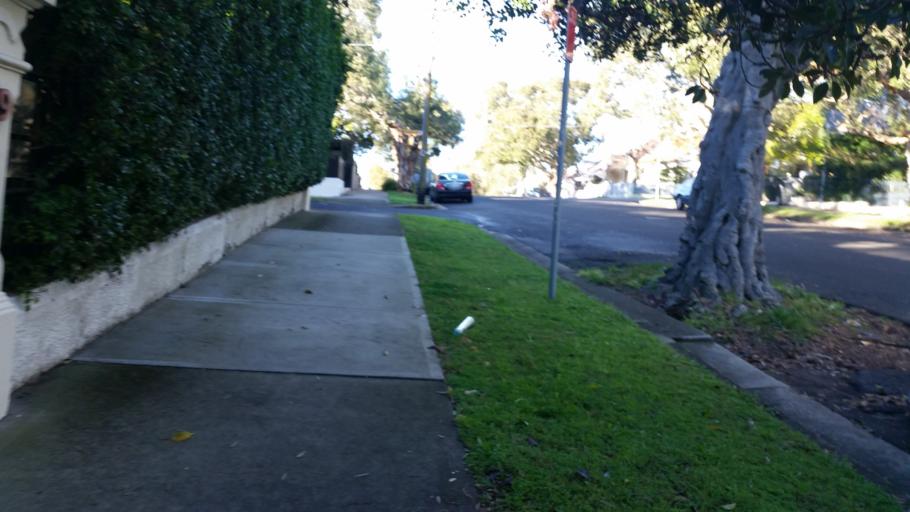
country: AU
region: New South Wales
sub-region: Waverley
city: Bronte
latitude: -33.9046
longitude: 151.2612
